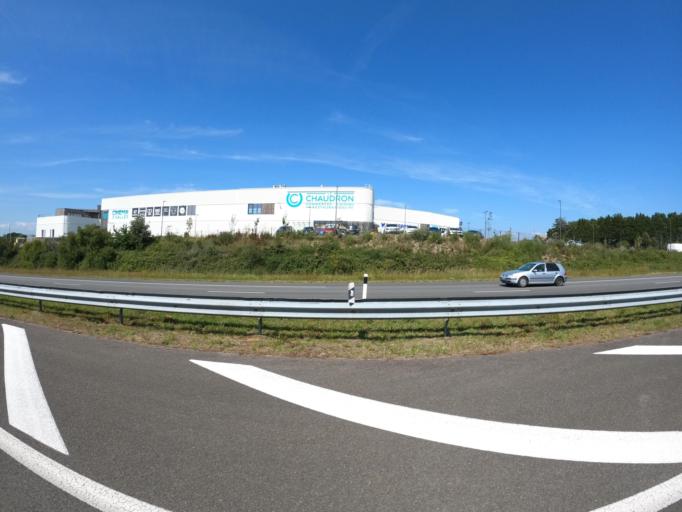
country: FR
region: Pays de la Loire
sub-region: Departement de la Loire-Atlantique
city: Pornic
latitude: 47.1113
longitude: -2.0754
